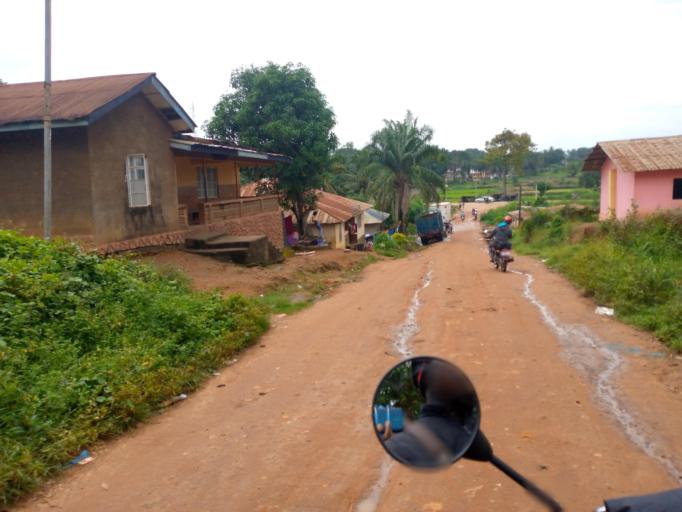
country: SL
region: Eastern Province
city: Kenema
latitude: 7.8602
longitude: -11.1913
